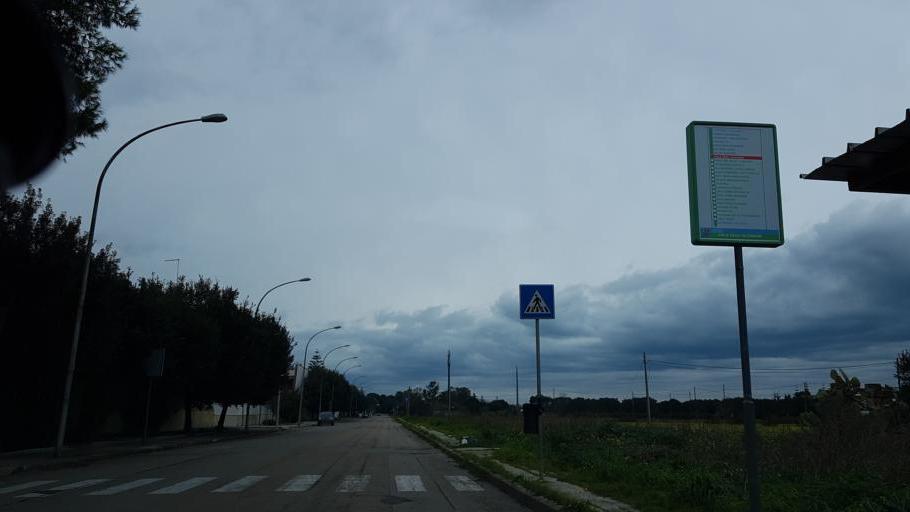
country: IT
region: Apulia
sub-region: Provincia di Brindisi
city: La Rosa
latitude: 40.6046
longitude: 17.9544
